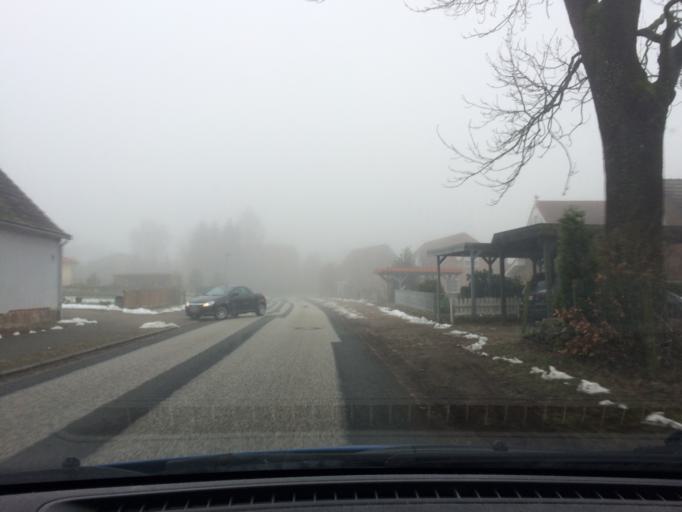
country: DE
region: Schleswig-Holstein
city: Juliusburg
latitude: 53.4143
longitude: 10.5049
